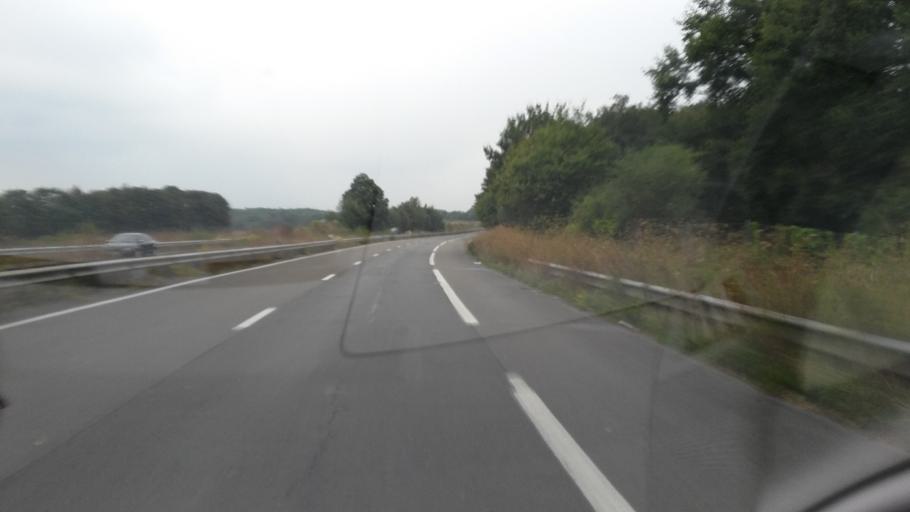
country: FR
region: Champagne-Ardenne
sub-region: Departement des Ardennes
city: Bazeilles
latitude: 49.6964
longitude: 5.0002
